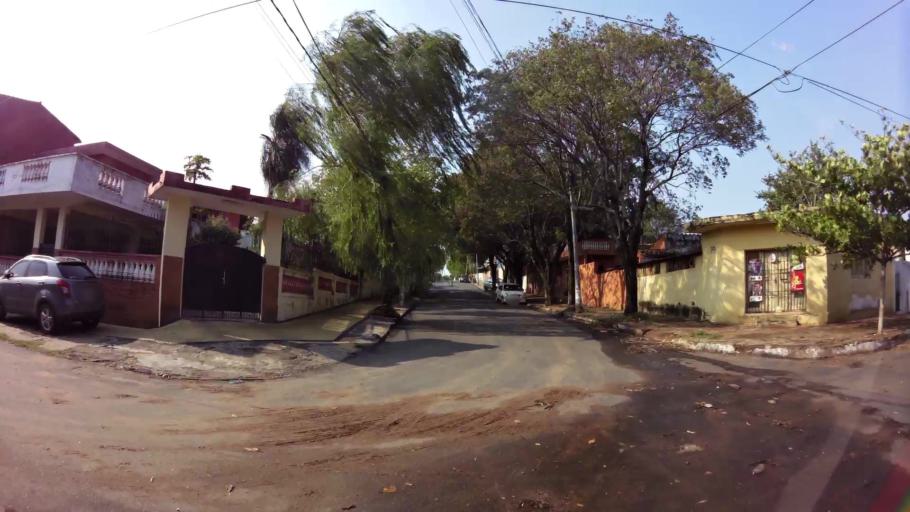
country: PY
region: Presidente Hayes
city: Nanawa
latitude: -25.2817
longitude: -57.6639
